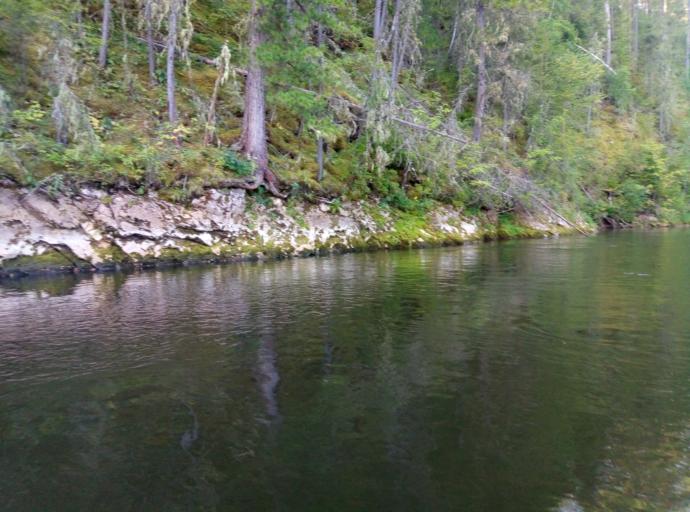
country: RU
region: Sverdlovsk
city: Karpinsk
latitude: 59.6028
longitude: 59.9938
